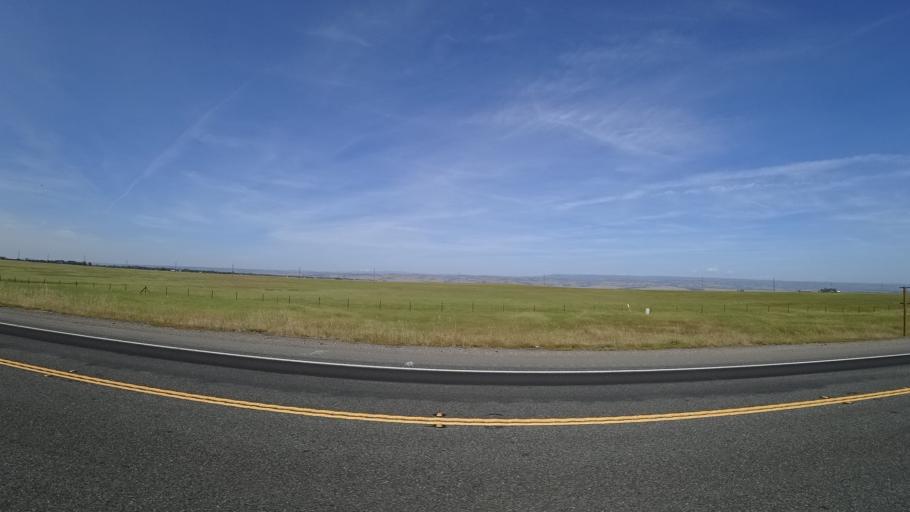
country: US
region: California
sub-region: Tehama County
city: Los Molinos
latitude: 39.9220
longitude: -122.0218
